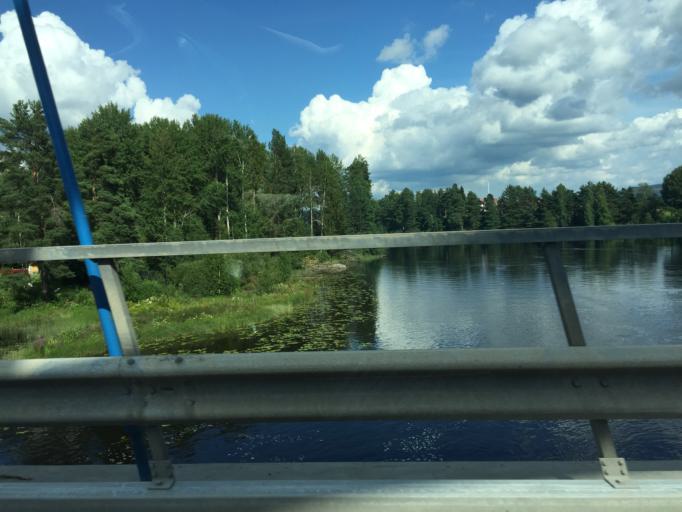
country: SE
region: Gaevleborg
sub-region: Bollnas Kommun
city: Bollnas
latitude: 61.3158
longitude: 16.4396
